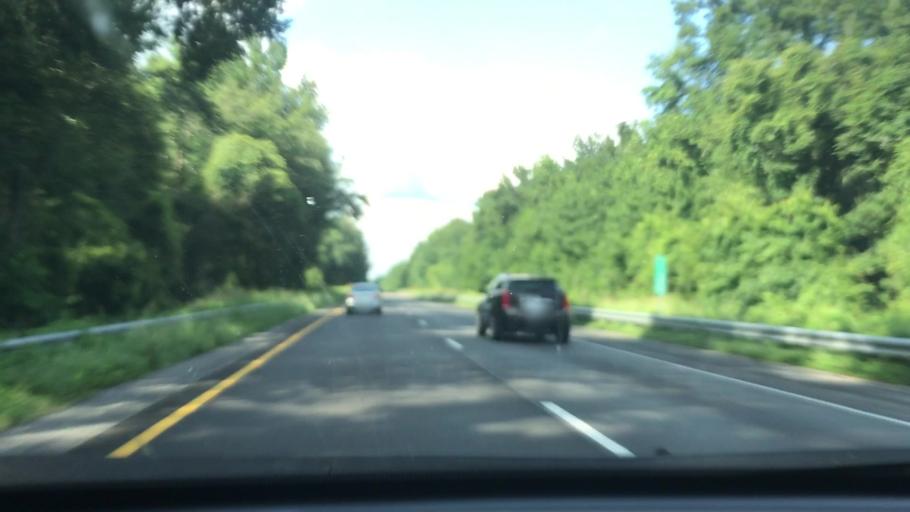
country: US
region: South Carolina
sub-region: Clarendon County
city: Manning
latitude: 33.8318
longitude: -80.1320
